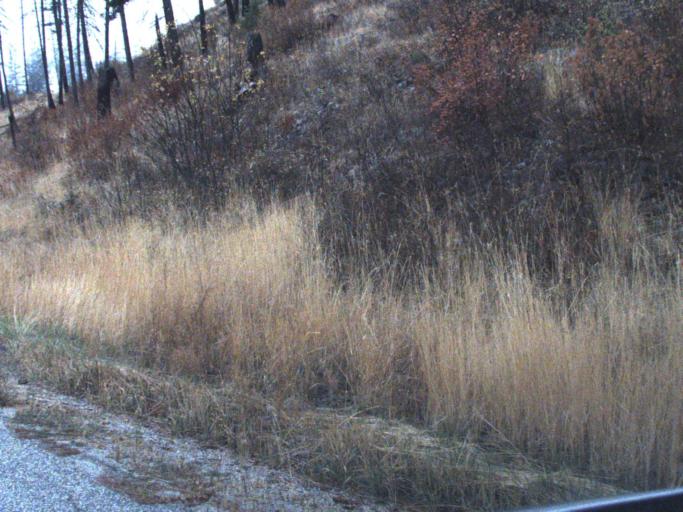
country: US
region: Washington
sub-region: Stevens County
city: Kettle Falls
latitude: 48.7553
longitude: -118.1346
